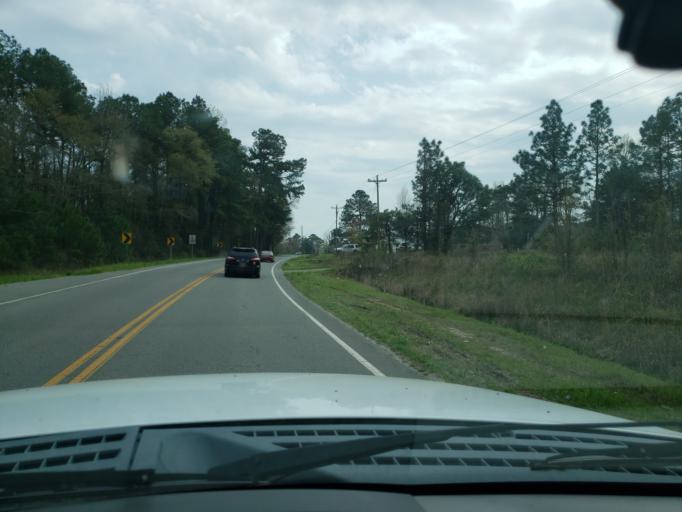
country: US
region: North Carolina
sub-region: Duplin County
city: Beulaville
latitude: 34.7828
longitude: -77.8368
